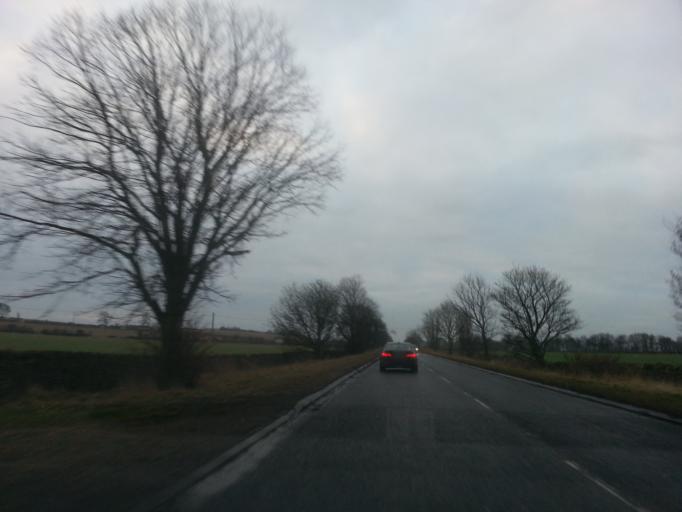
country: GB
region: England
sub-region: County Durham
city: Hamsterley
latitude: 54.6923
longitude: -1.7856
